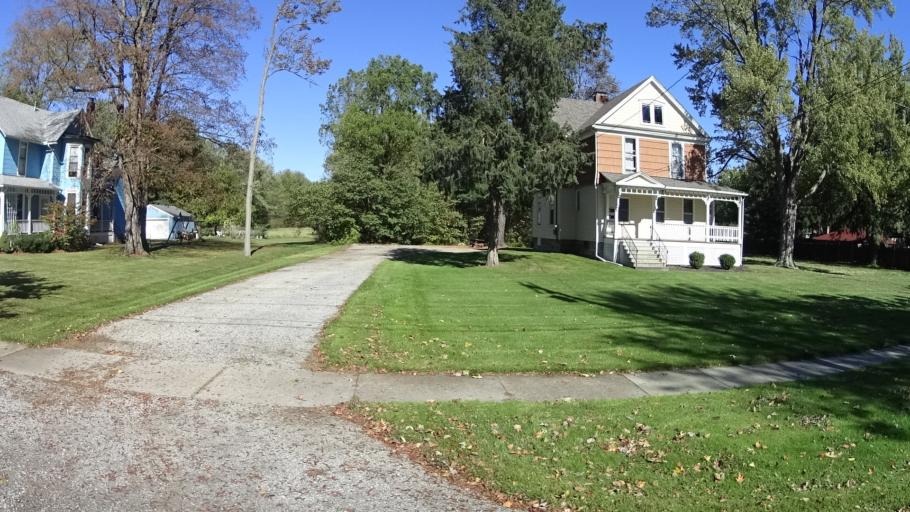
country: US
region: Ohio
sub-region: Lorain County
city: Oberlin
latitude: 41.2943
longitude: -82.2297
